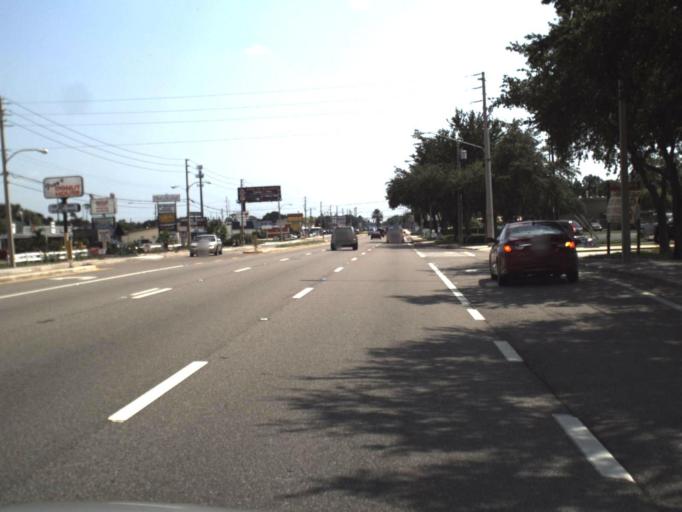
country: US
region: Florida
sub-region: Pinellas County
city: Kenneth City
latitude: 27.8124
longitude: -82.7287
